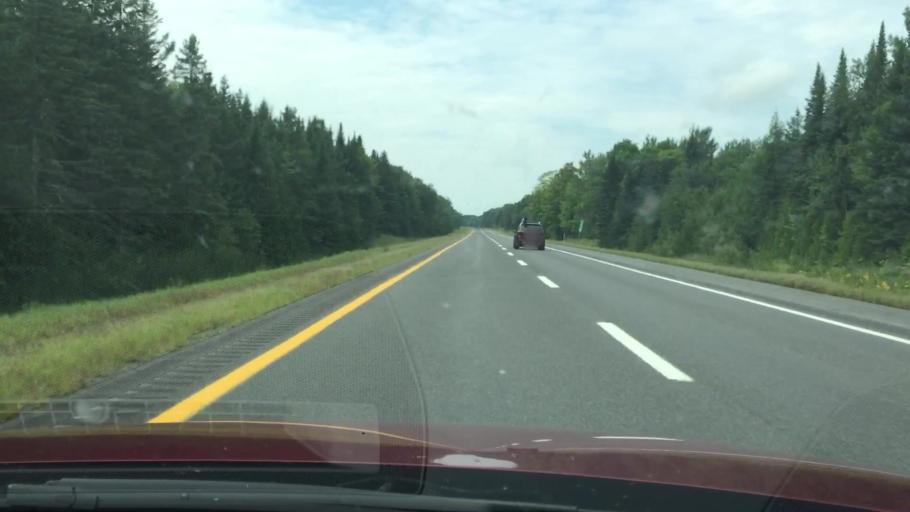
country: US
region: Maine
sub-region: Aroostook County
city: Houlton
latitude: 46.1387
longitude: -67.9183
